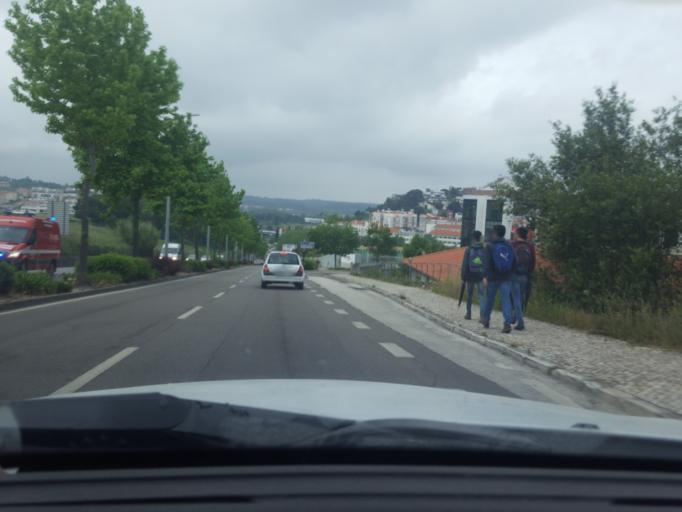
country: PT
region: Leiria
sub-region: Leiria
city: Leiria
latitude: 39.7357
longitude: -8.8108
